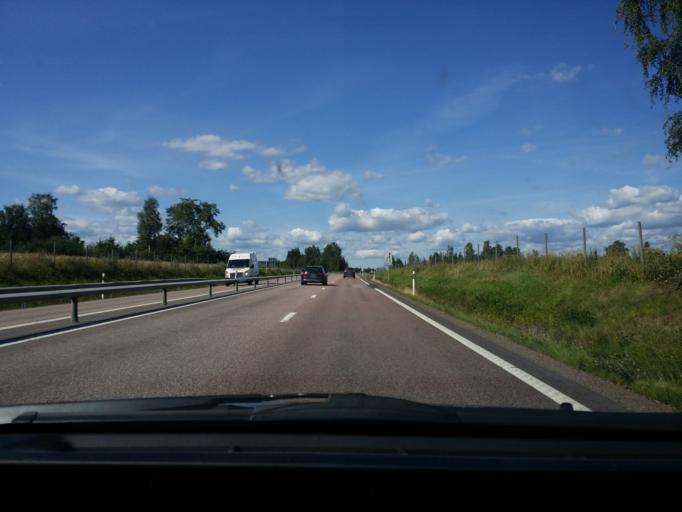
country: SE
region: Dalarna
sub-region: Hedemora Kommun
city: Brunna
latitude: 60.2672
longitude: 16.0071
